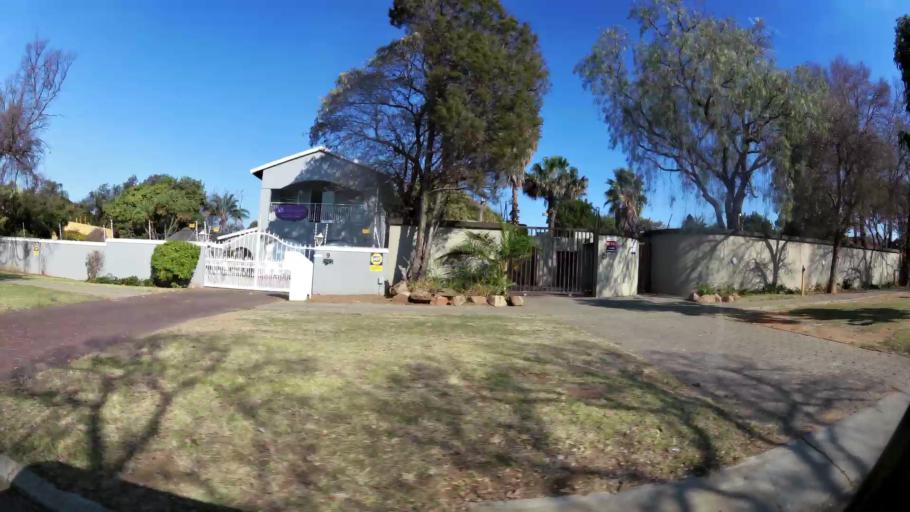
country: ZA
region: Gauteng
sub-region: City of Johannesburg Metropolitan Municipality
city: Roodepoort
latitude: -26.1099
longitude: 27.9533
